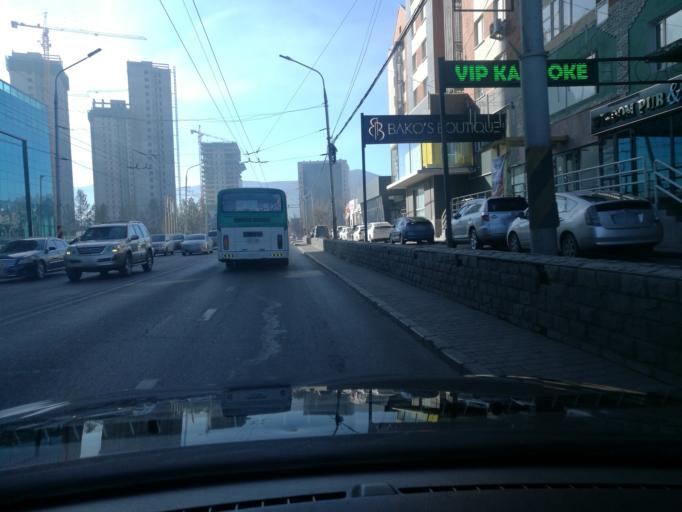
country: MN
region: Ulaanbaatar
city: Ulaanbaatar
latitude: 47.9046
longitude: 106.9115
